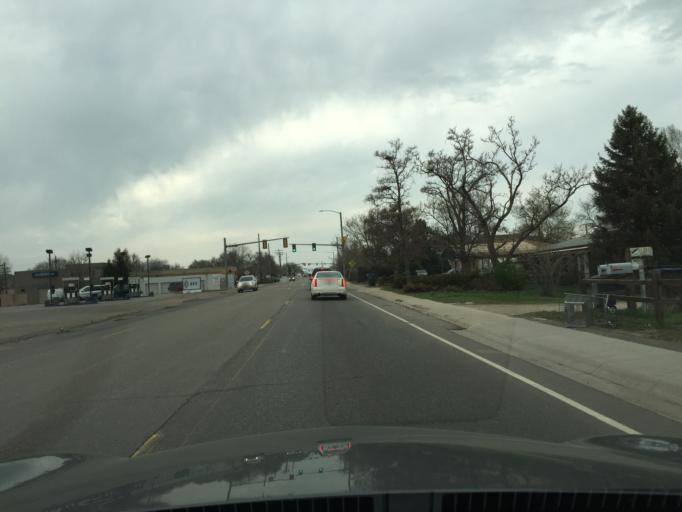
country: US
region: Colorado
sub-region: Boulder County
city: Lafayette
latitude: 40.0003
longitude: -105.0971
